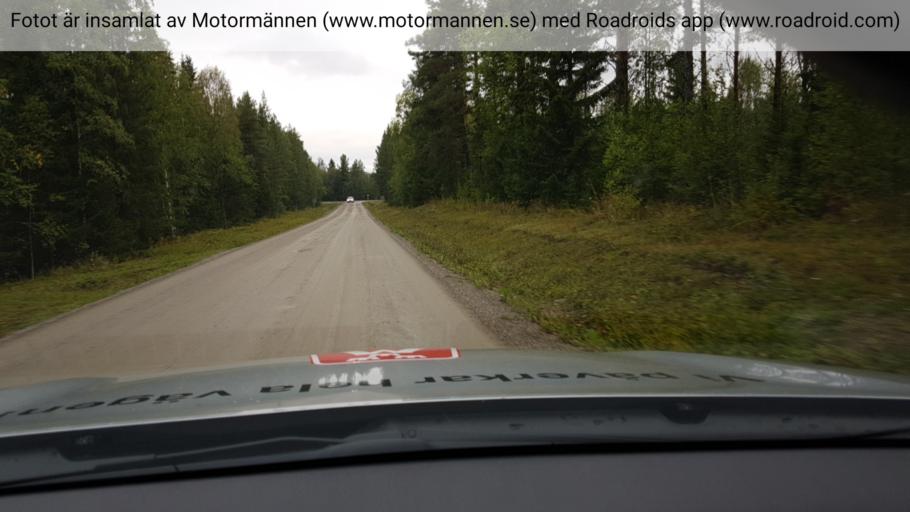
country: SE
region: Jaemtland
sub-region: Braecke Kommun
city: Braecke
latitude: 62.7796
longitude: 15.4743
